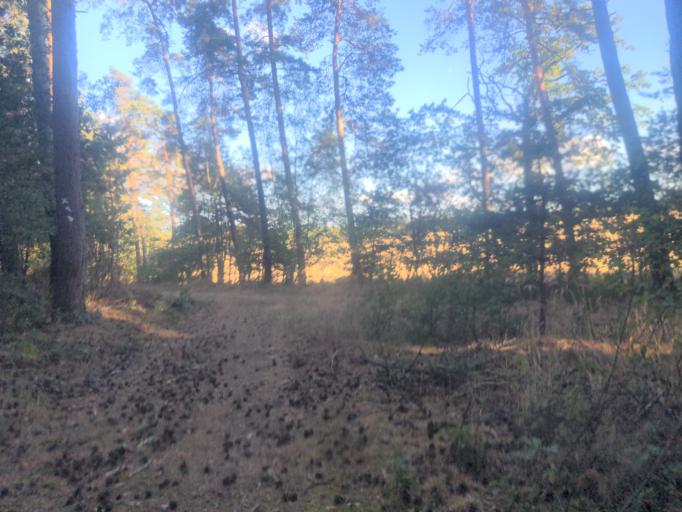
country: DE
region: Lower Saxony
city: Neu Darchau
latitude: 53.2150
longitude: 10.8672
